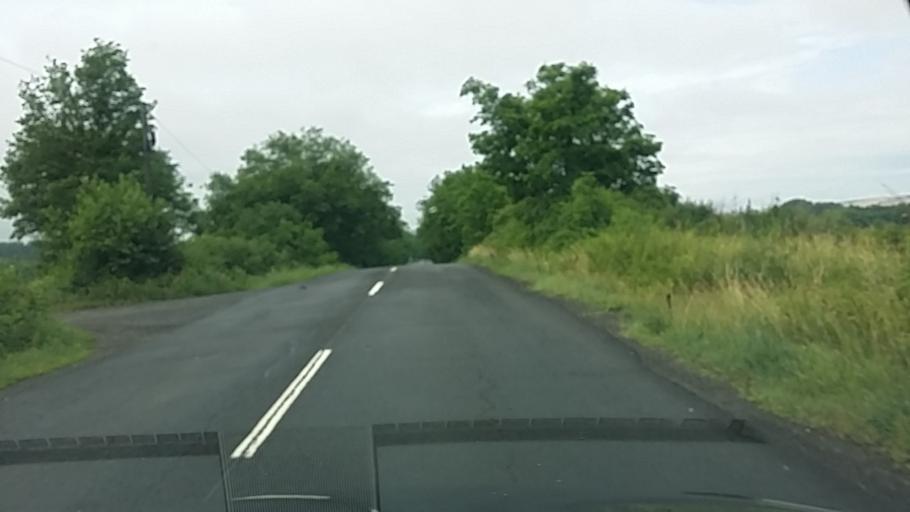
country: SK
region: Nitriansky
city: Sahy
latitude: 47.9878
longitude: 18.8170
